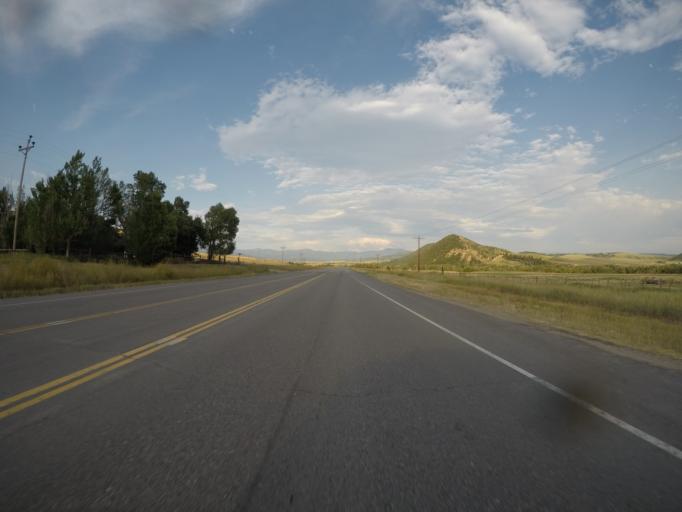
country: US
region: Colorado
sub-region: Routt County
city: Steamboat Springs
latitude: 40.4857
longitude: -107.0070
